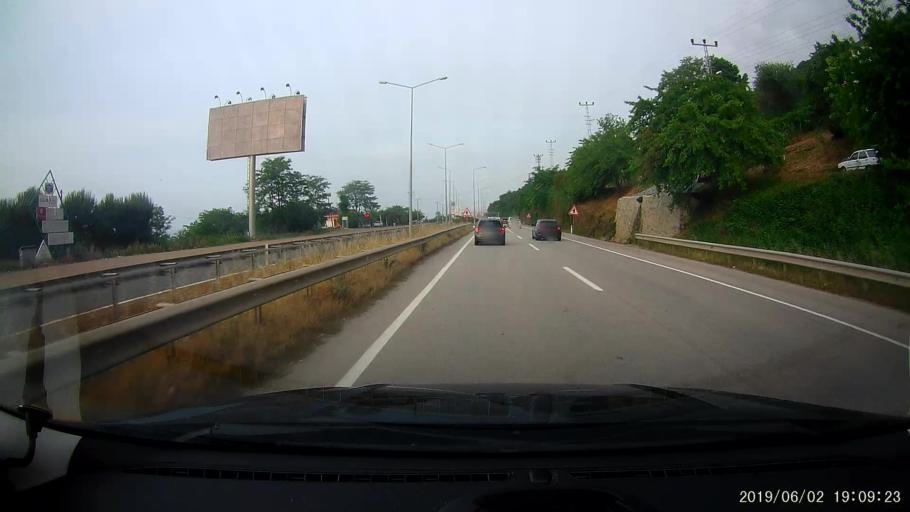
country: TR
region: Ordu
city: Gulyali
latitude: 40.9730
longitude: 38.0273
